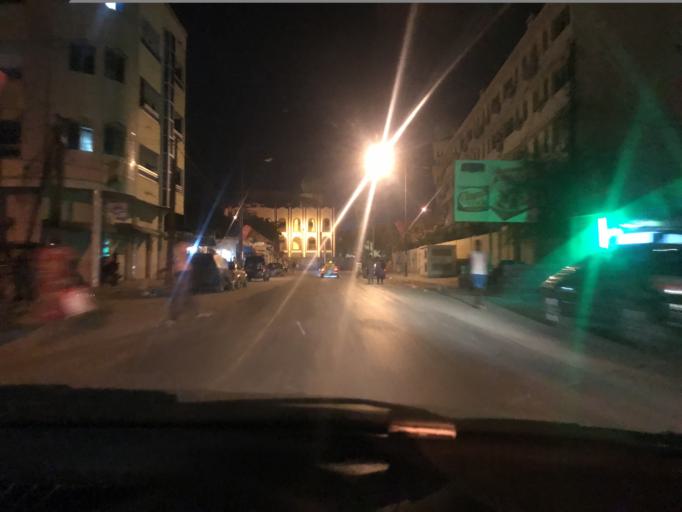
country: SN
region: Dakar
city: Dakar
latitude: 14.6750
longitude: -17.4497
